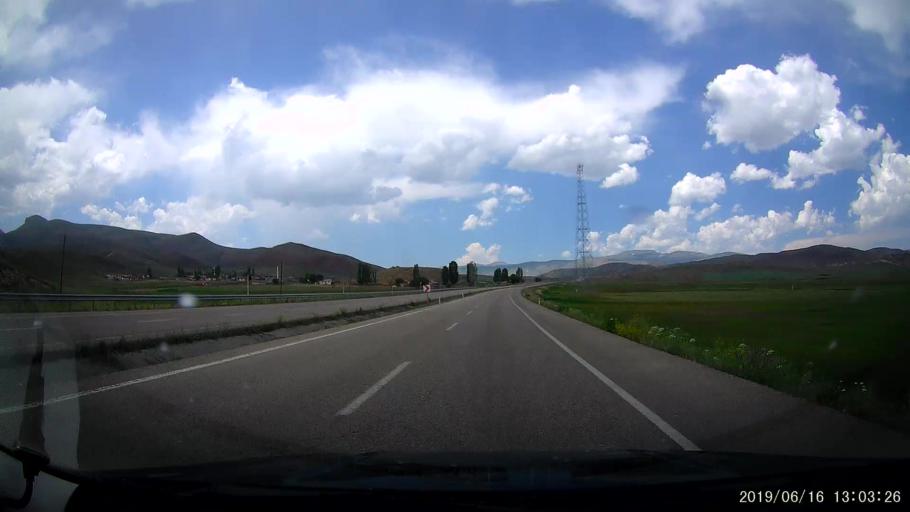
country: TR
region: Agri
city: Sulucem
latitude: 39.5813
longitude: 43.7905
